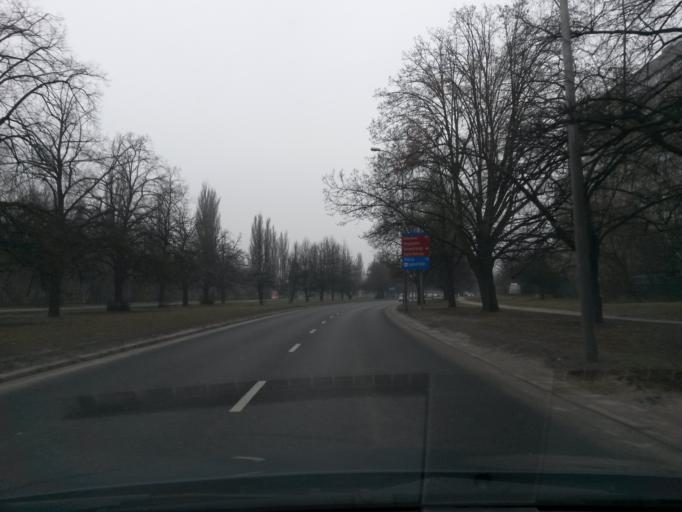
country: PL
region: Masovian Voivodeship
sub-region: Warszawa
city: Ochota
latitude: 52.2132
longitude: 20.9885
